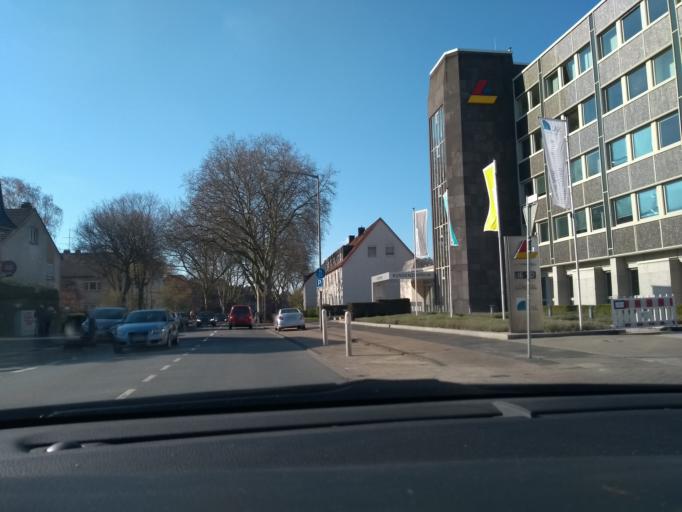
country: DE
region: North Rhine-Westphalia
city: Lunen
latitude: 51.6212
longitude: 7.5176
